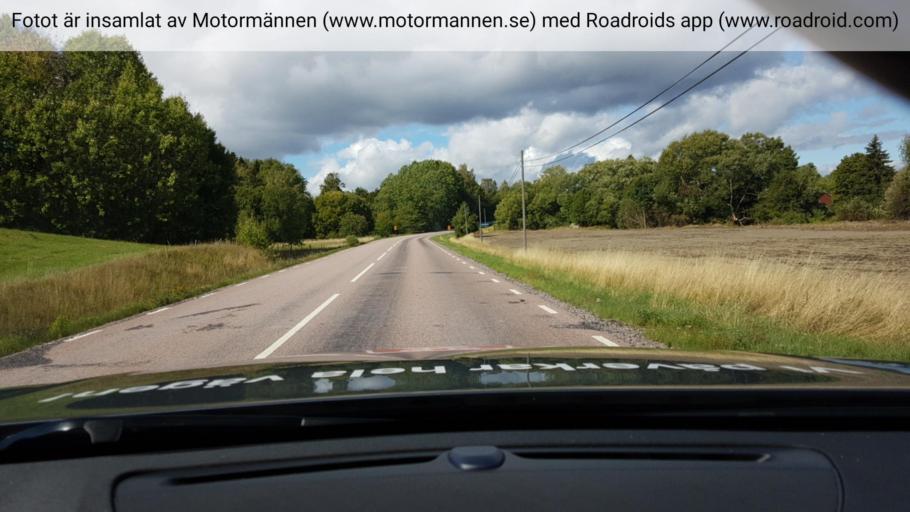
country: SE
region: Soedermanland
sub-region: Strangnas Kommun
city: Stallarholmen
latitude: 59.3543
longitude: 17.2138
